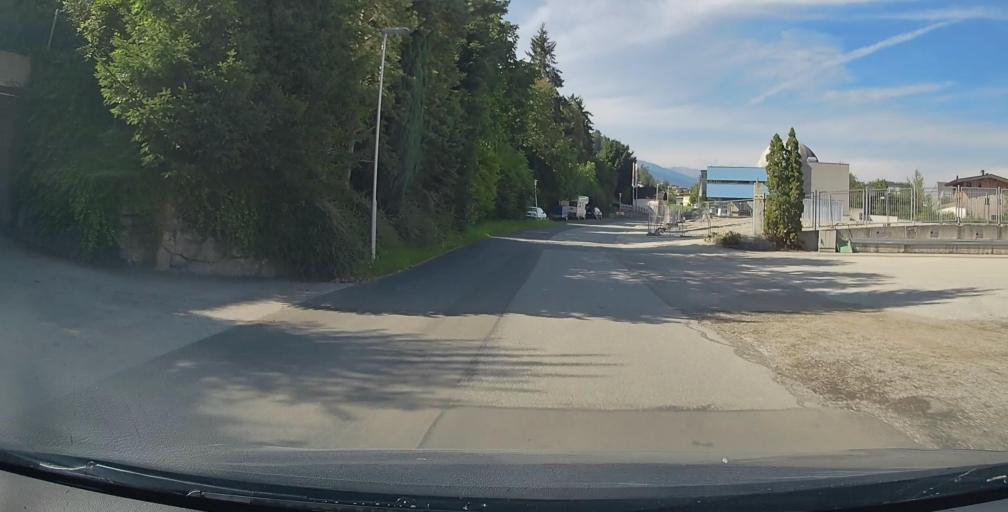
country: AT
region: Tyrol
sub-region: Politischer Bezirk Schwaz
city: Stans
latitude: 47.3546
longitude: 11.7289
